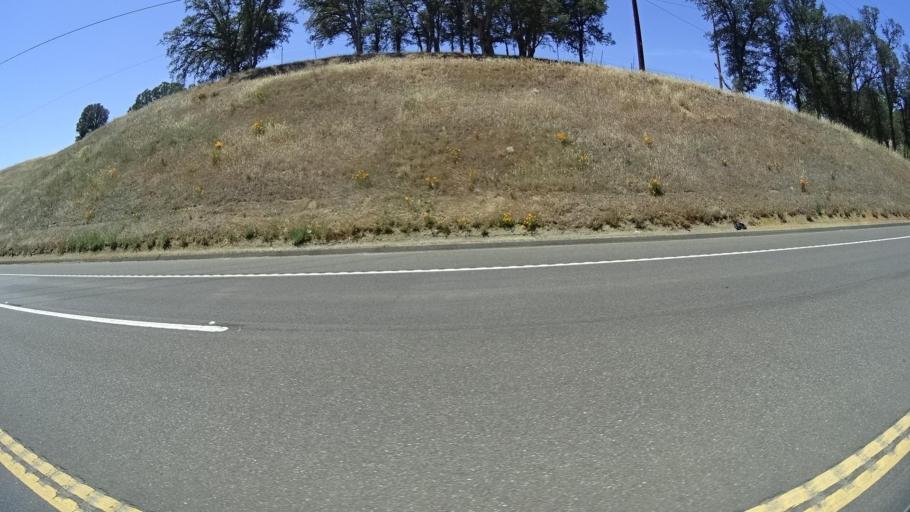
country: US
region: California
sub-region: Lake County
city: Clearlake
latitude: 38.9797
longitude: -122.6127
